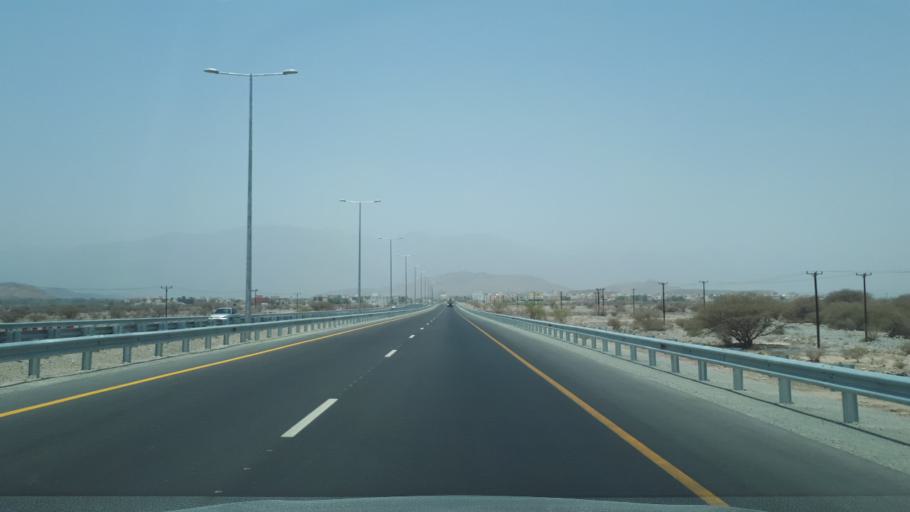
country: OM
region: Al Batinah
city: Rustaq
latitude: 23.4655
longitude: 57.4413
